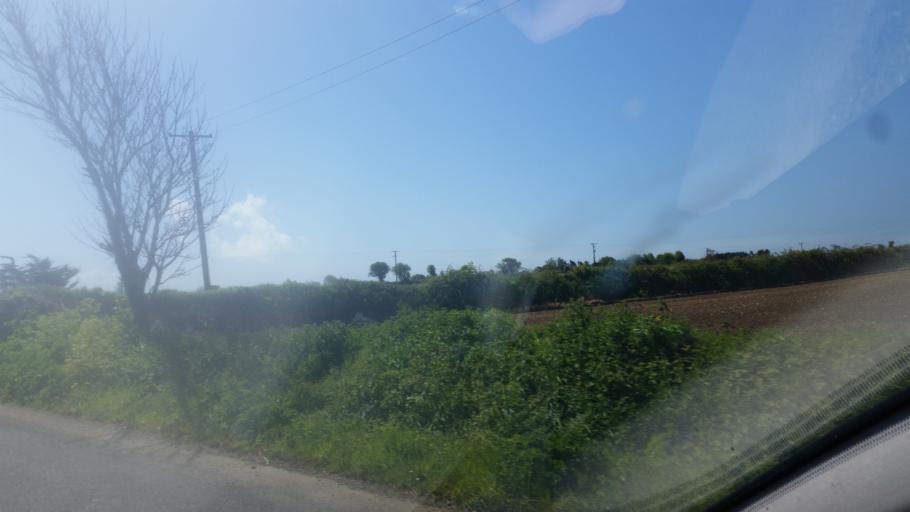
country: IE
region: Munster
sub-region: Waterford
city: Dunmore East
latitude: 52.1983
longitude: -6.8572
